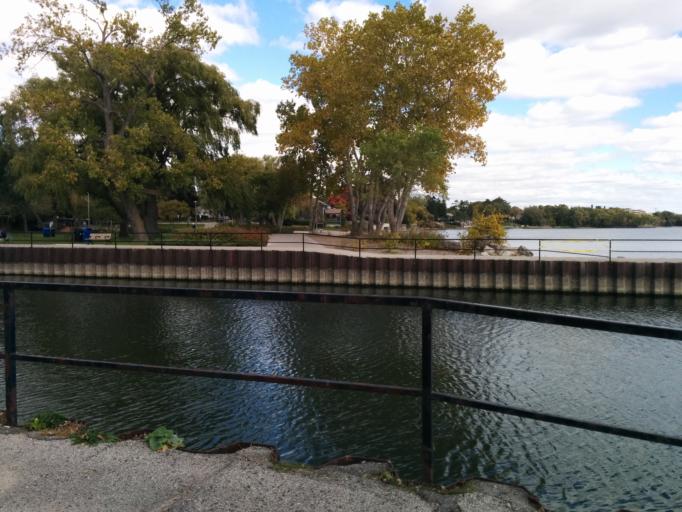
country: CA
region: Ontario
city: Etobicoke
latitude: 43.5847
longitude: -79.5415
